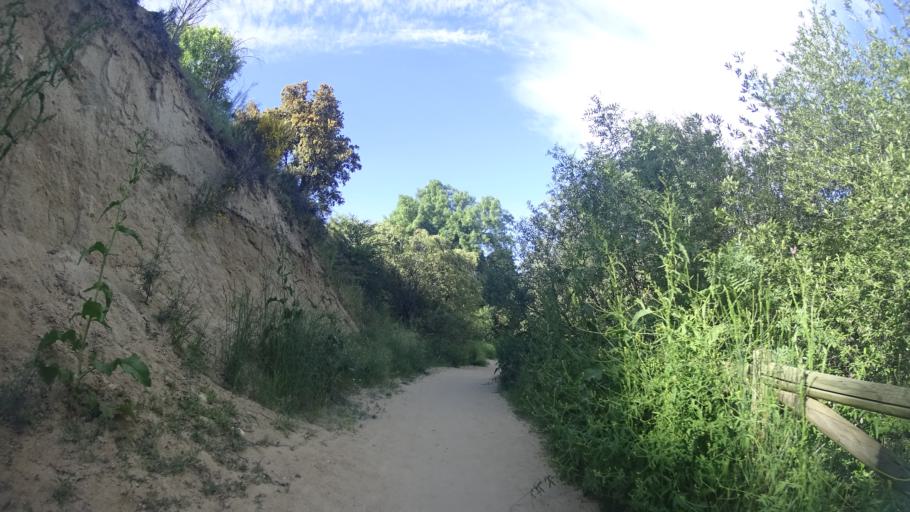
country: ES
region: Madrid
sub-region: Provincia de Madrid
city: Villanueva del Pardillo
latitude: 40.5175
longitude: -3.9401
